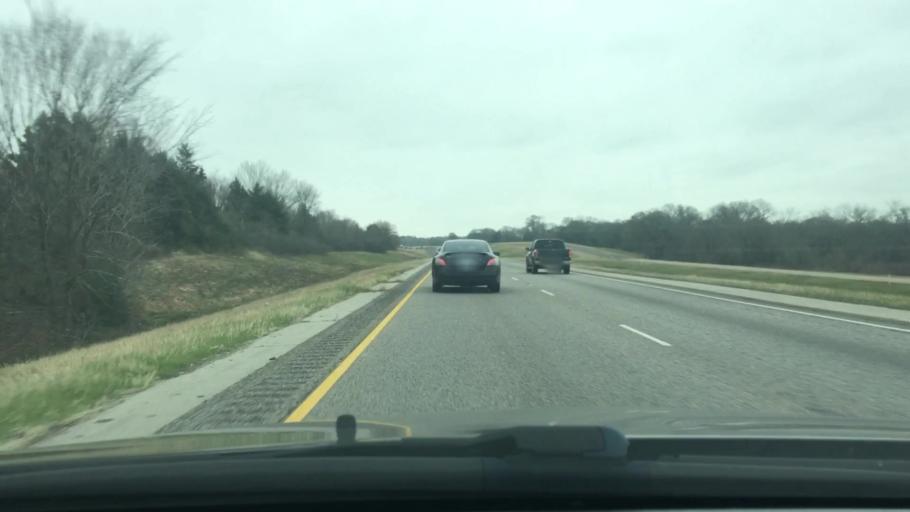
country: US
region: Texas
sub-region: Freestone County
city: Fairfield
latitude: 31.7951
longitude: -96.2529
